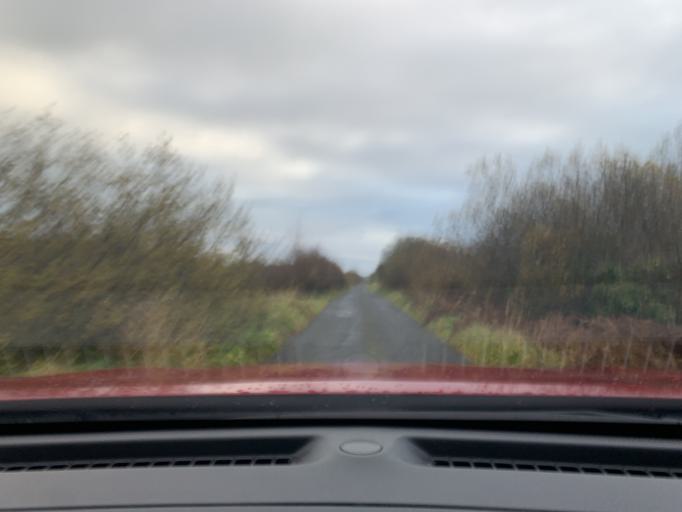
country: IE
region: Connaught
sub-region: Sligo
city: Ballymote
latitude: 54.0163
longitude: -8.5106
